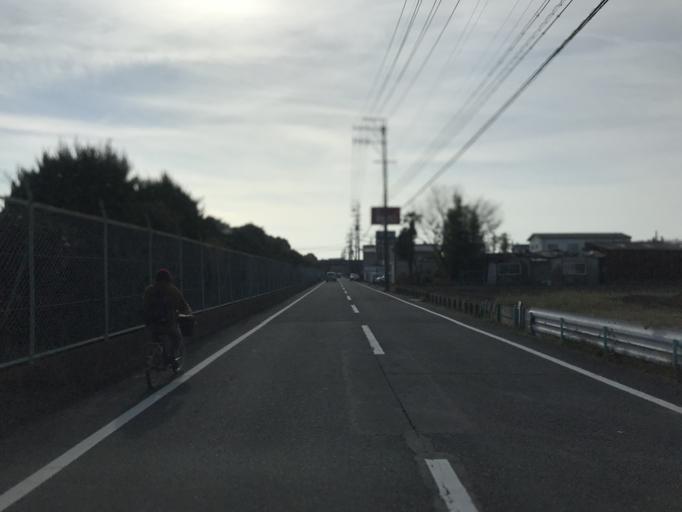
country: JP
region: Aichi
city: Inazawa
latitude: 35.2260
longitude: 136.8288
